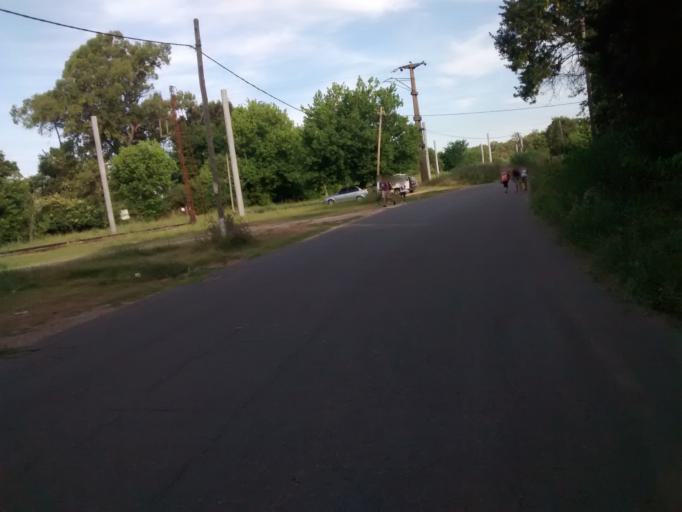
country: AR
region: Buenos Aires
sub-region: Partido de La Plata
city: La Plata
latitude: -34.8373
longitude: -58.0942
